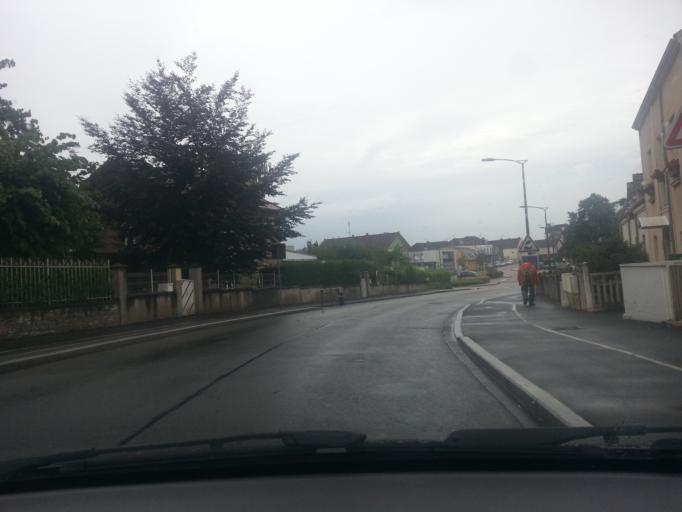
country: FR
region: Bourgogne
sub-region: Departement de Saone-et-Loire
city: Montchanin
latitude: 46.7506
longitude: 4.4719
